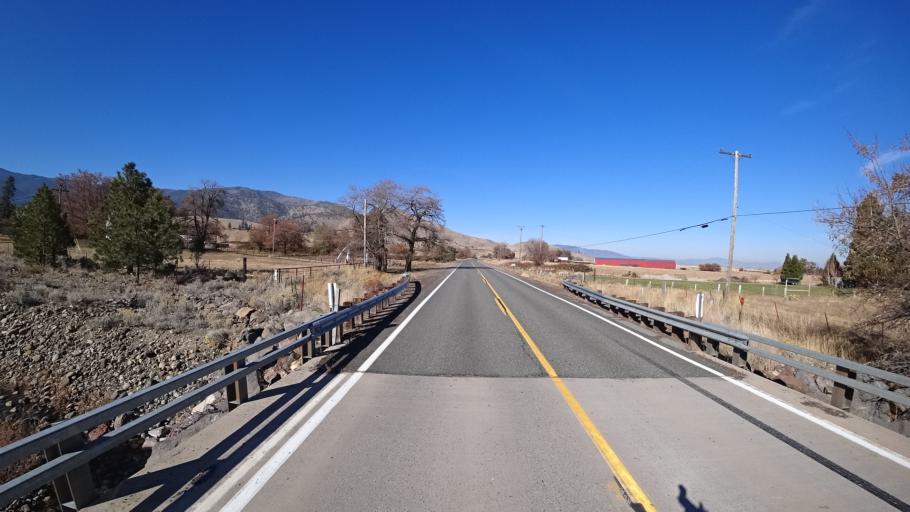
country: US
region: California
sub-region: Siskiyou County
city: Weed
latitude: 41.4480
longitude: -122.4497
